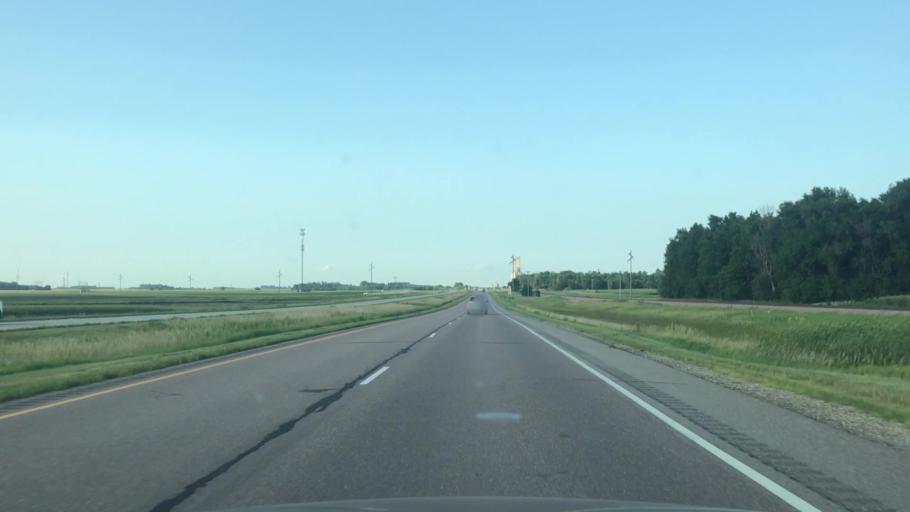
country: US
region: Minnesota
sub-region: Jackson County
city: Lakefield
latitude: 43.7580
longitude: -95.3792
